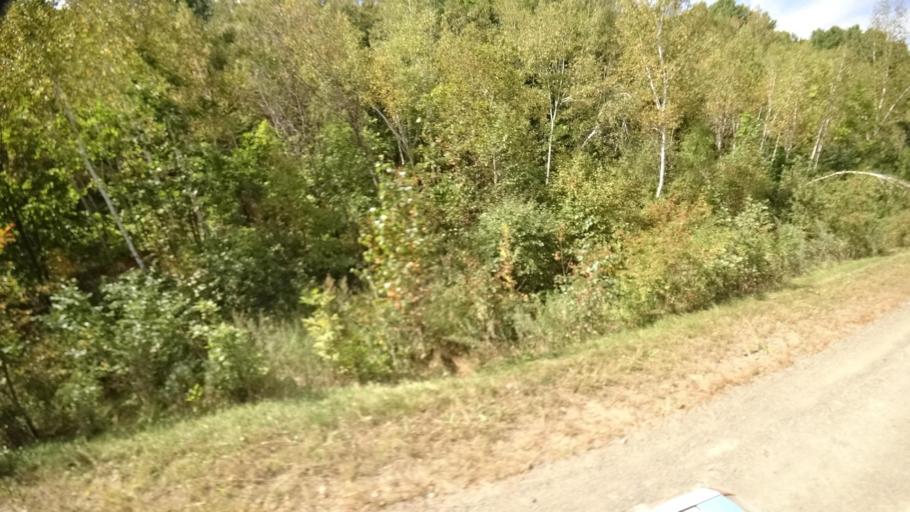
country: RU
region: Primorskiy
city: Yakovlevka
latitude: 44.7019
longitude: 133.6520
